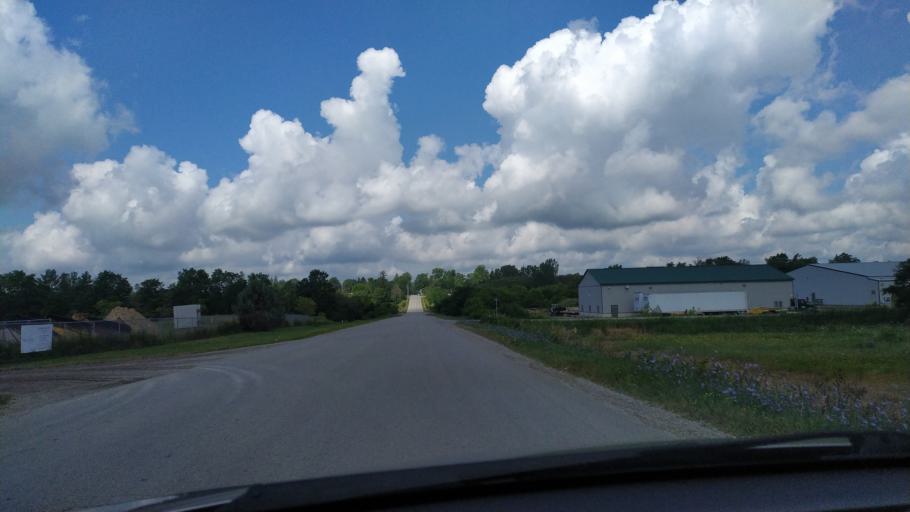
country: CA
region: Ontario
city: Huron East
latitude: 43.4583
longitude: -81.1999
